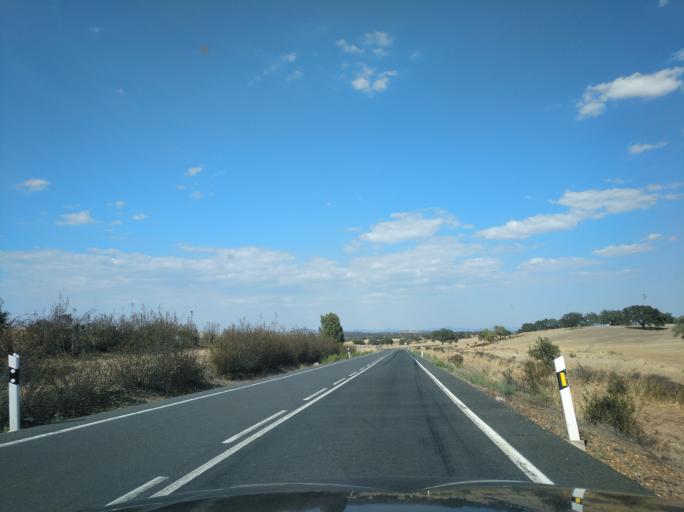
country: ES
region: Andalusia
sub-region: Provincia de Huelva
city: Cabezas Rubias
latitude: 37.6424
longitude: -7.1277
